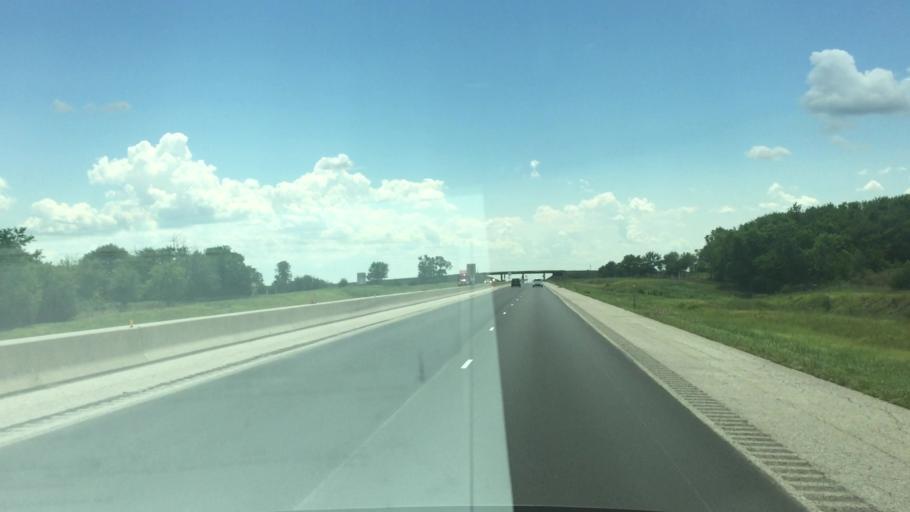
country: US
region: Kansas
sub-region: Osage County
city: Osage City
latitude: 38.7002
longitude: -95.9896
